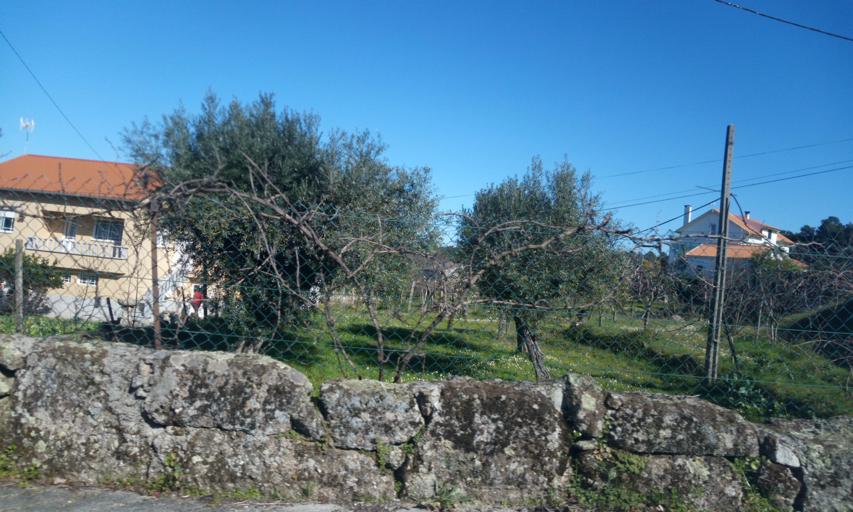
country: PT
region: Guarda
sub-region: Fornos de Algodres
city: Fornos de Algodres
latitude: 40.5191
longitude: -7.6129
